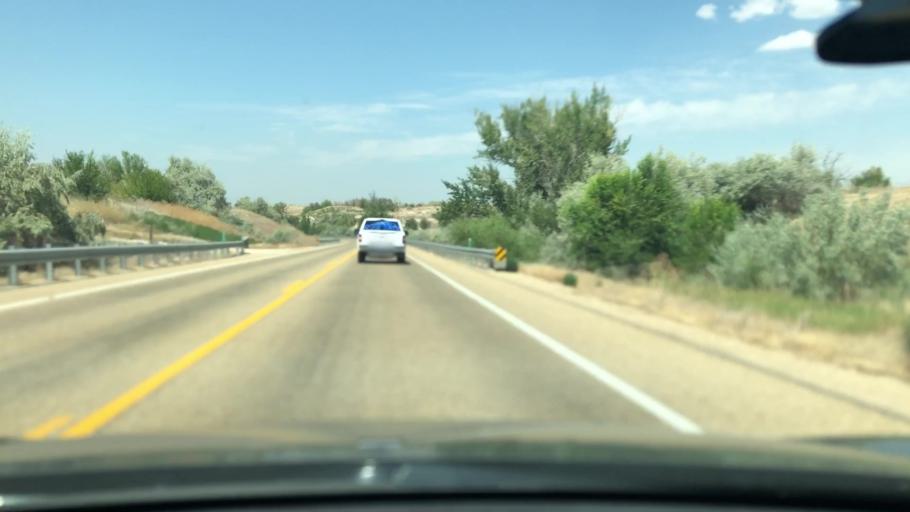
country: US
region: Idaho
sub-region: Canyon County
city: Wilder
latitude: 43.7152
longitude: -116.9118
